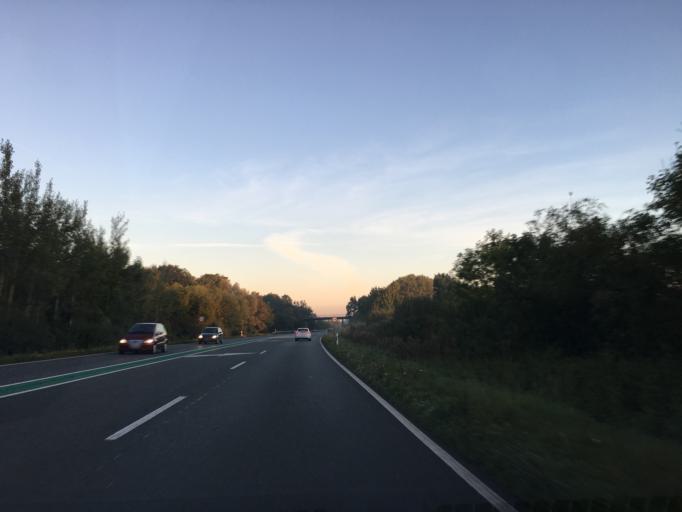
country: DE
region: North Rhine-Westphalia
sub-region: Regierungsbezirk Munster
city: Altenberge
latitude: 52.0805
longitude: 7.4198
